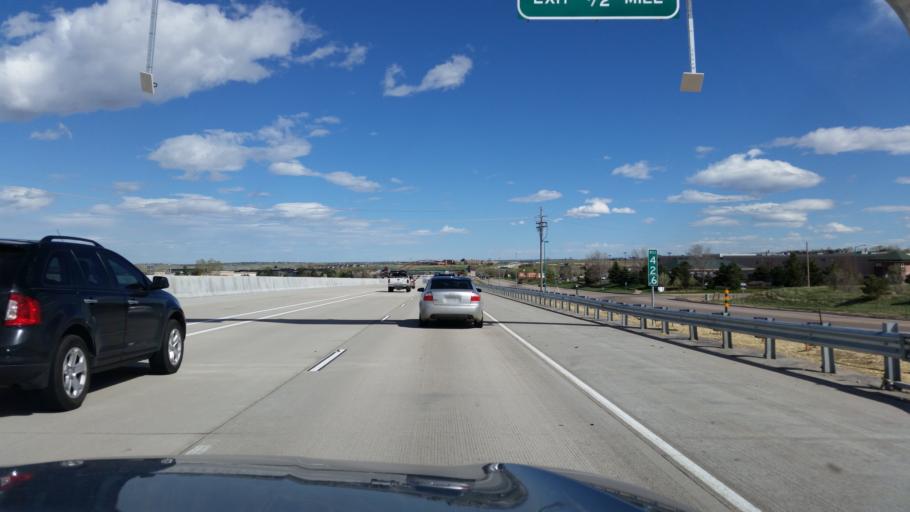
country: US
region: Colorado
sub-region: Boulder County
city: Superior
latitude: 39.9616
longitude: -105.1764
